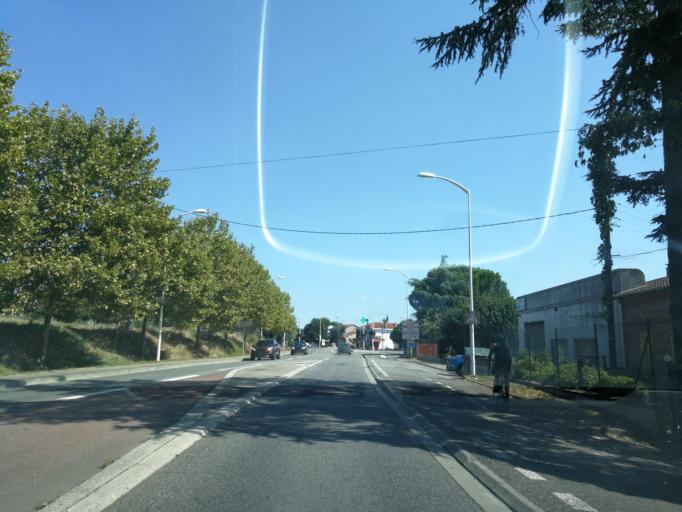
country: FR
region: Midi-Pyrenees
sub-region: Departement de la Haute-Garonne
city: Balma
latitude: 43.5862
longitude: 1.5227
